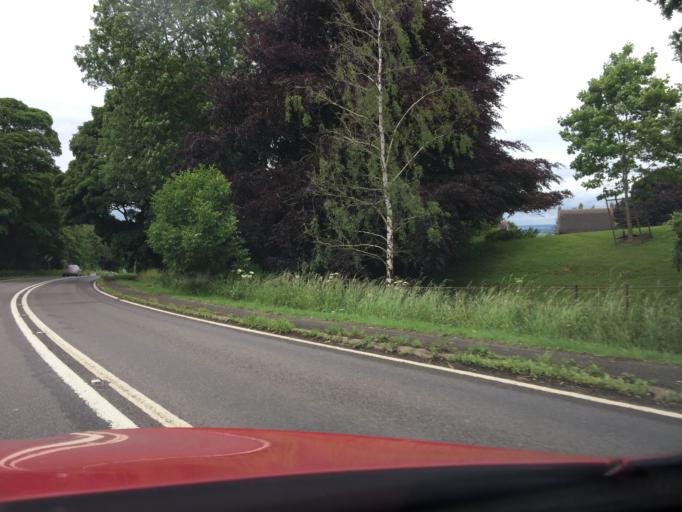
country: GB
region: England
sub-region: Northamptonshire
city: Daventry
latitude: 52.2458
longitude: -1.2153
